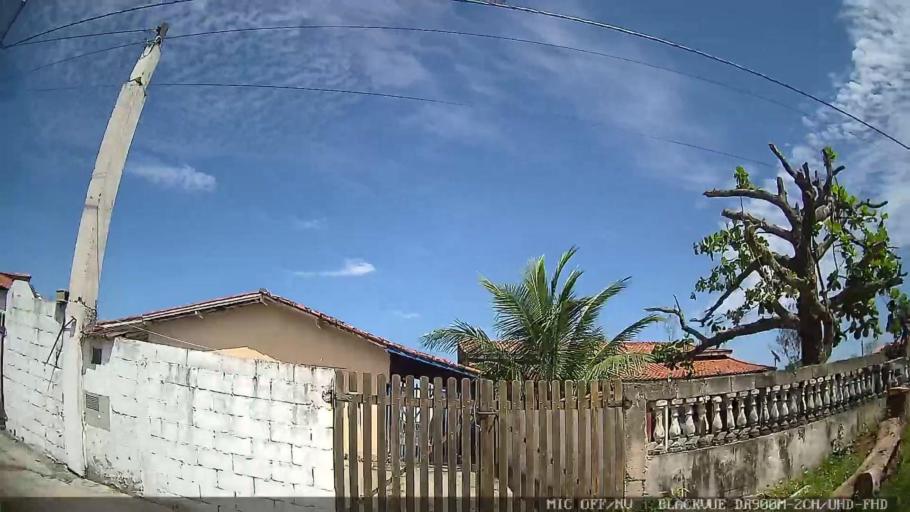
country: BR
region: Sao Paulo
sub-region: Iguape
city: Iguape
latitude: -24.8081
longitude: -47.6403
